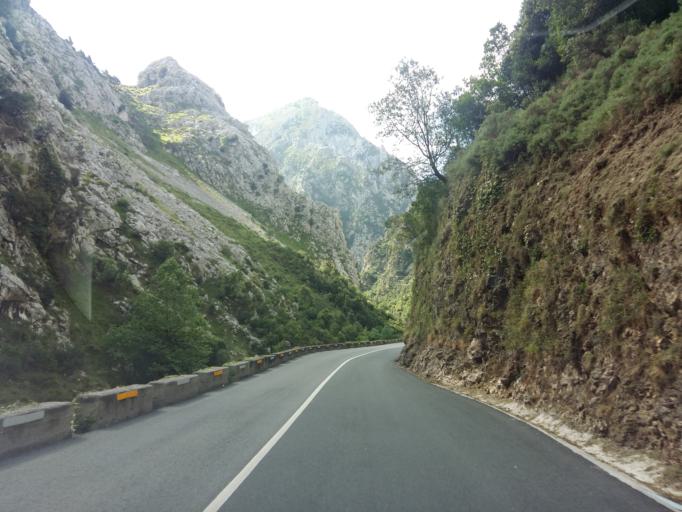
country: ES
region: Cantabria
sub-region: Provincia de Cantabria
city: Tresviso
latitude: 43.2730
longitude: -4.6366
